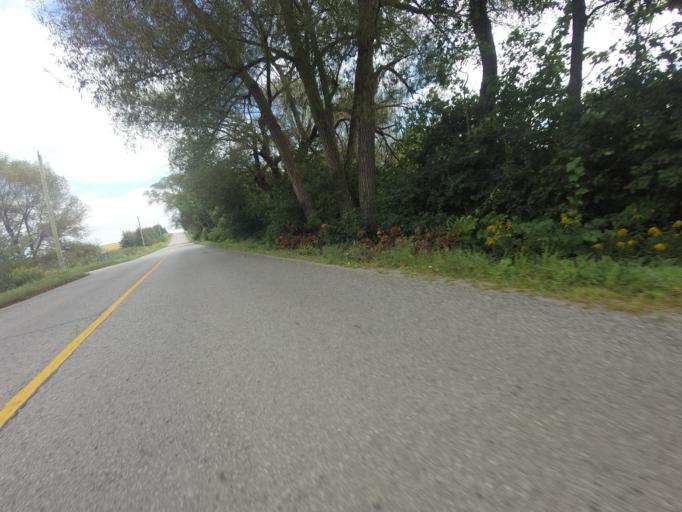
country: CA
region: Ontario
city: Uxbridge
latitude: 44.1247
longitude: -79.1374
